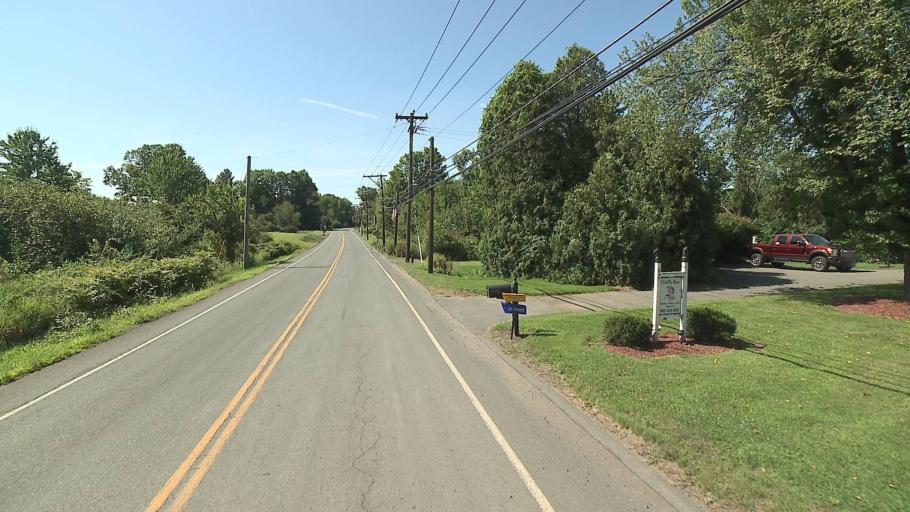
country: US
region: Connecticut
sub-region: Hartford County
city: Tariffville
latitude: 41.9347
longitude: -72.7308
